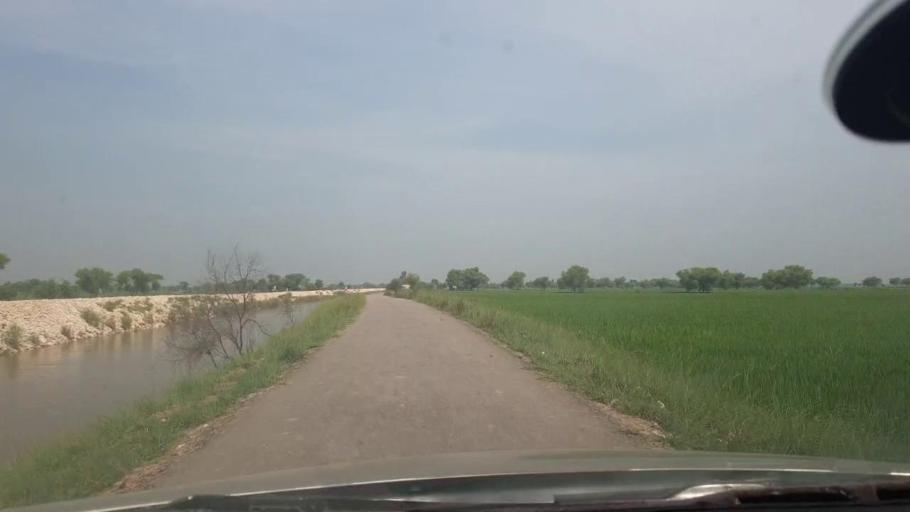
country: PK
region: Sindh
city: Jacobabad
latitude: 28.2898
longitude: 68.4817
